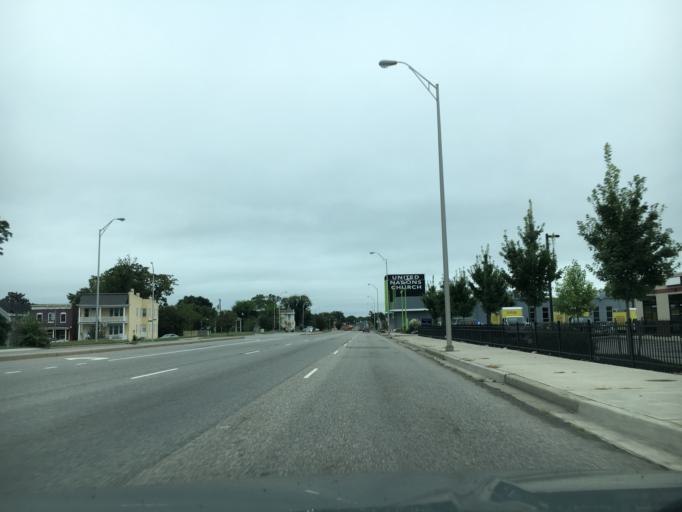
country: US
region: Virginia
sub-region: City of Richmond
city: Richmond
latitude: 37.5221
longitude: -77.4511
